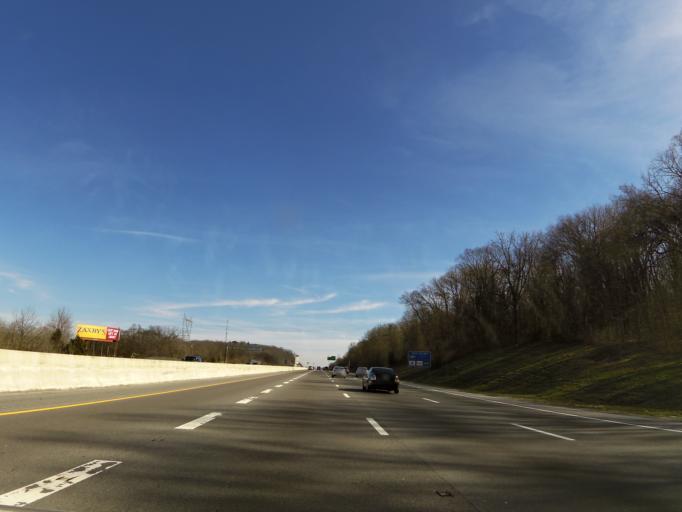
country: US
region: Tennessee
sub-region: Rutherford County
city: La Vergne
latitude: 36.0290
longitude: -86.6370
